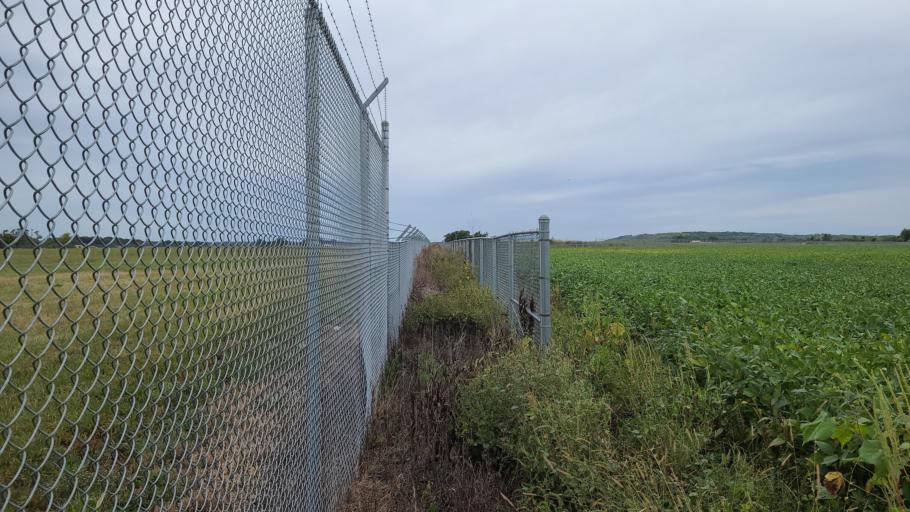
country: US
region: Kansas
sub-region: Douglas County
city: Lawrence
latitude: 39.0158
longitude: -95.2141
